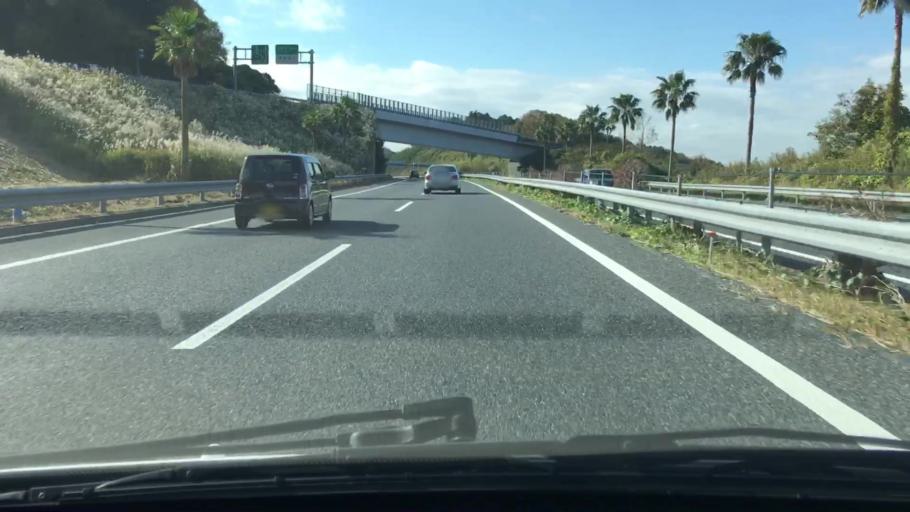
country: JP
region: Chiba
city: Kisarazu
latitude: 35.3550
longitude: 139.9498
